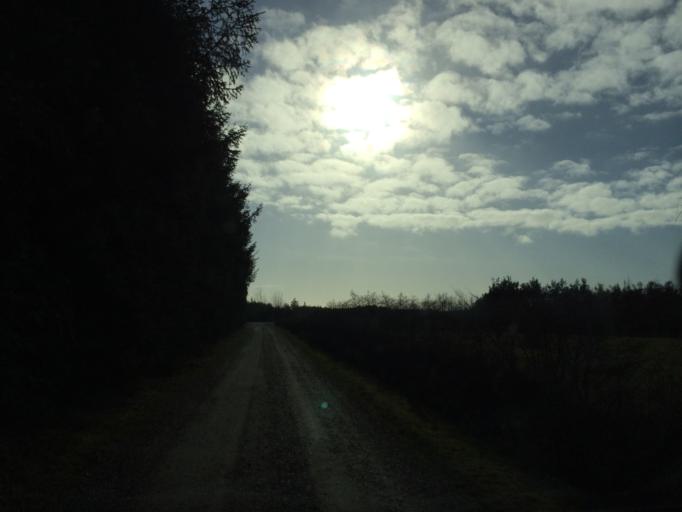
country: DK
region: Central Jutland
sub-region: Holstebro Kommune
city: Ulfborg
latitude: 56.2688
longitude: 8.3312
